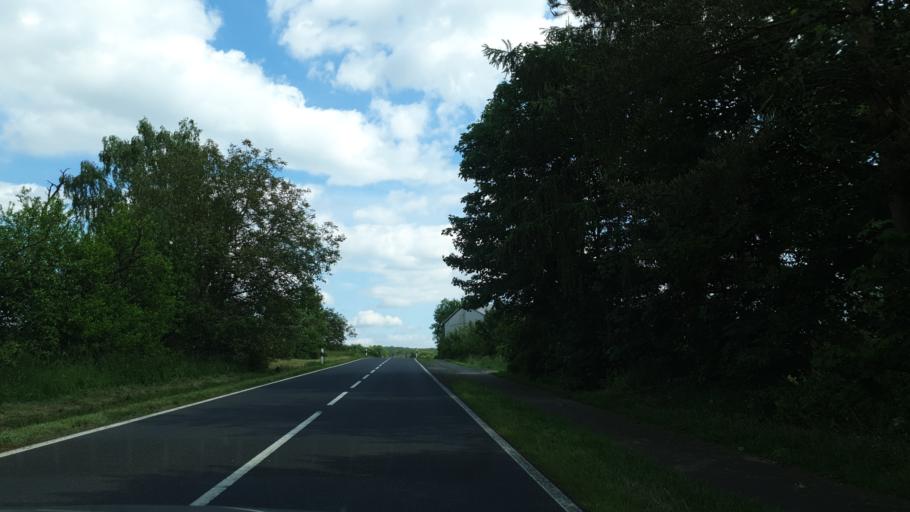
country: DE
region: Rheinland-Pfalz
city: Wolferlingen
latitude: 50.5640
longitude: 7.8541
